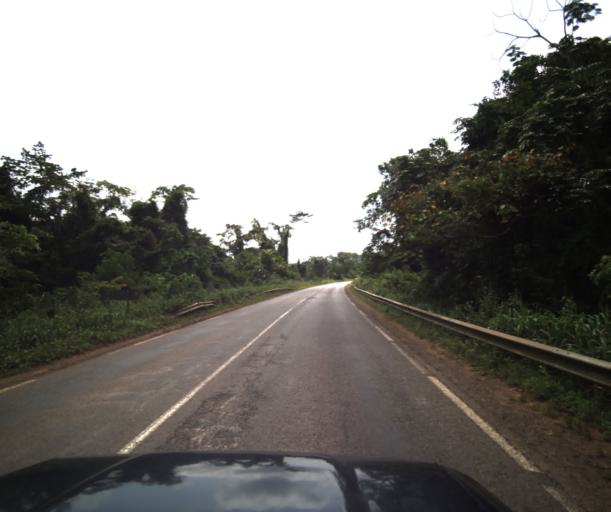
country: CM
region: Centre
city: Eseka
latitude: 3.8819
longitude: 10.8089
